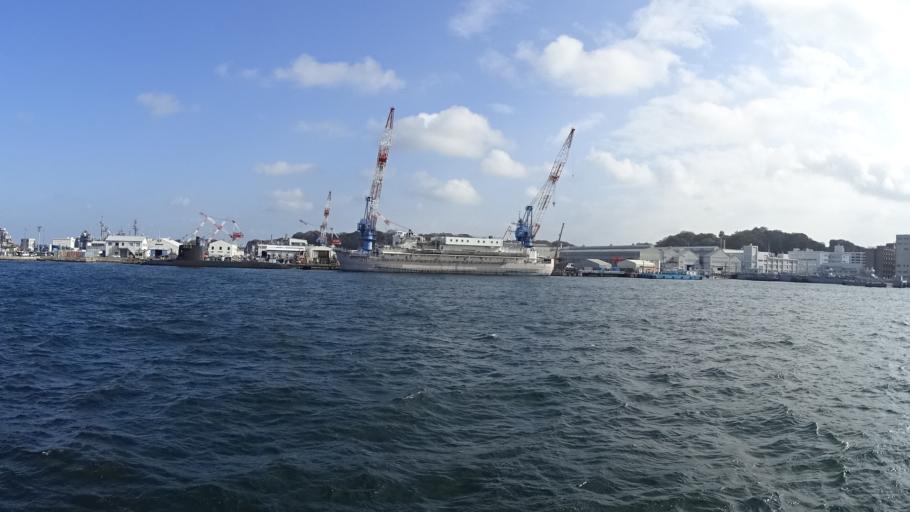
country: JP
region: Kanagawa
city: Yokosuka
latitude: 35.2882
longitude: 139.6560
